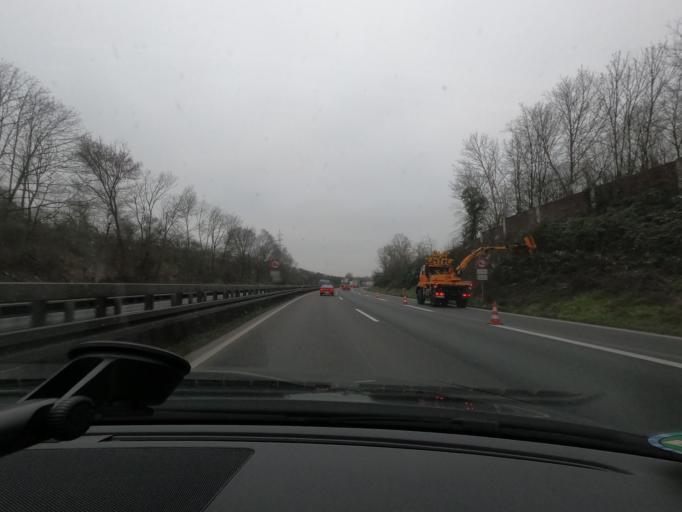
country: DE
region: North Rhine-Westphalia
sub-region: Regierungsbezirk Dusseldorf
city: Monchengladbach
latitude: 51.1731
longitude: 6.4053
